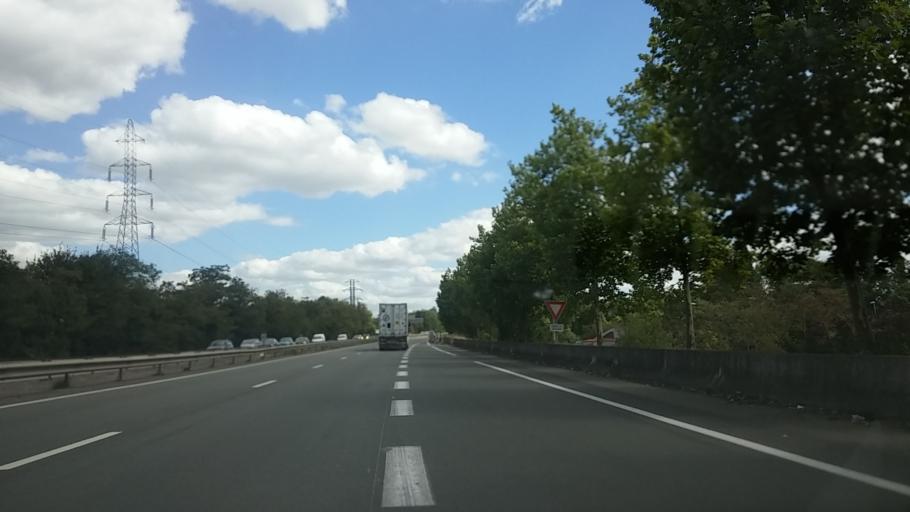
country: FR
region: Ile-de-France
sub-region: Departement des Yvelines
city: Fontenay-le-Fleury
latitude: 48.7944
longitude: 2.0494
